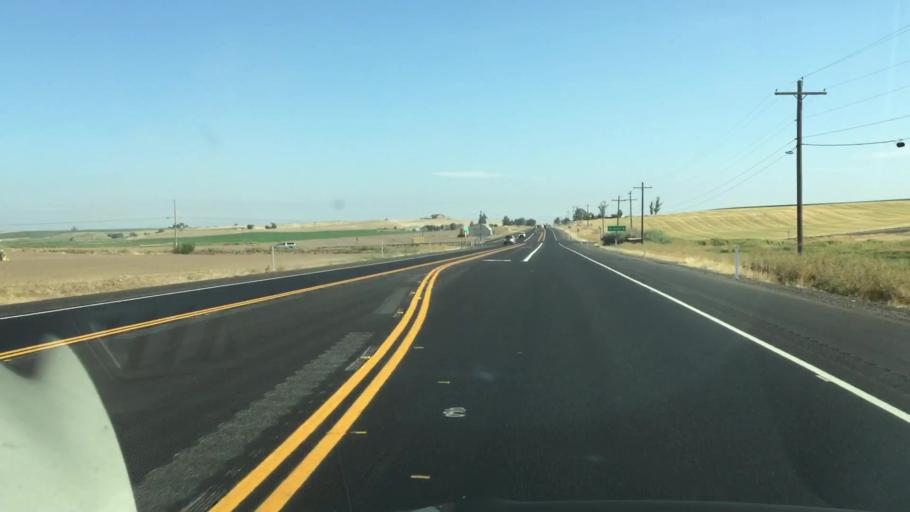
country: US
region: Oregon
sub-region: Jefferson County
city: Culver
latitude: 44.5185
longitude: -121.1826
